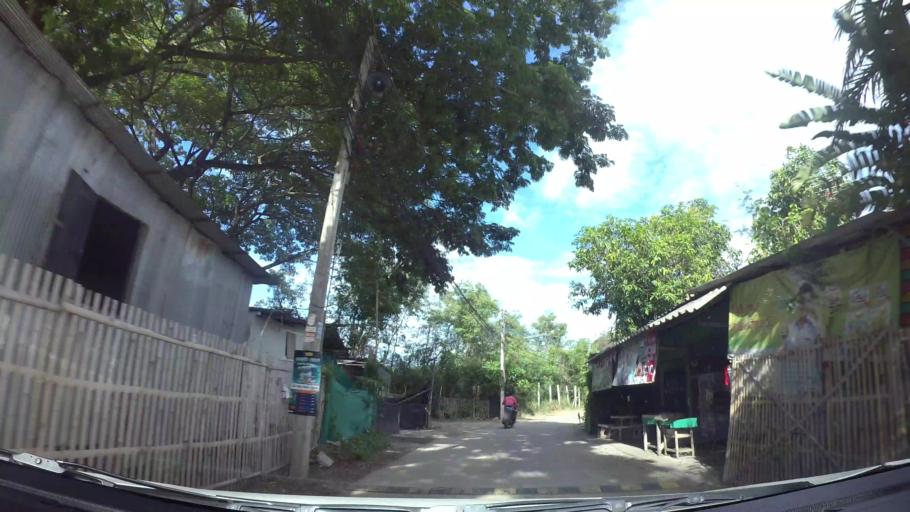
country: TH
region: Chiang Mai
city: Saraphi
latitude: 18.7492
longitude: 99.0280
